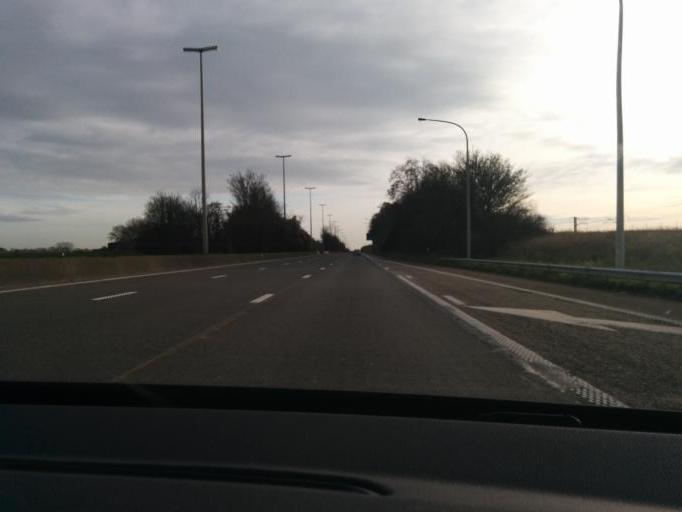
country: BE
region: Flanders
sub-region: Provincie Vlaams-Brabant
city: Tienen
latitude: 50.7486
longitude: 4.9568
